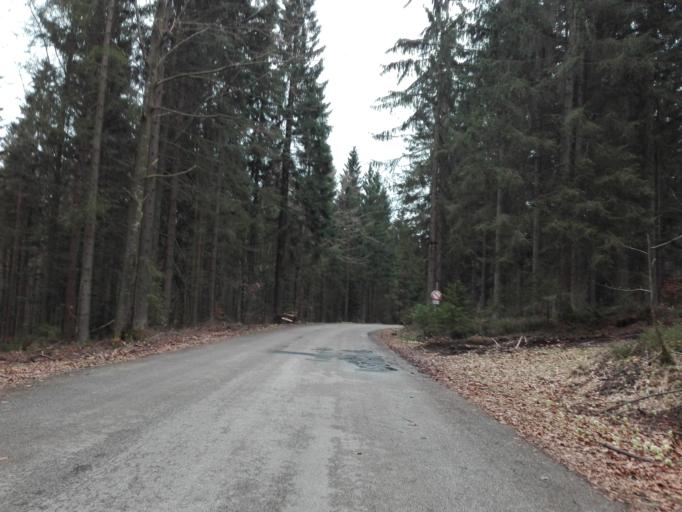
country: AT
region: Upper Austria
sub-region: Politischer Bezirk Rohrbach
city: Aigen im Muehlkreis
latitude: 48.7003
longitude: 13.9714
